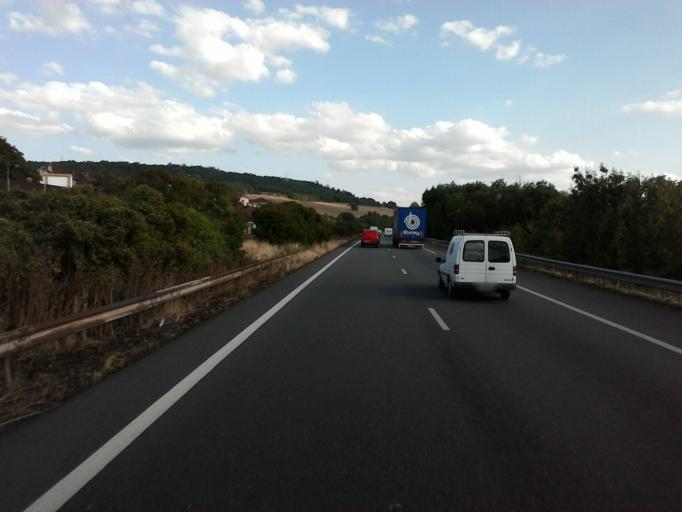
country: FR
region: Lorraine
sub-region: Departement de Meurthe-et-Moselle
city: Custines
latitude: 48.7856
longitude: 6.1432
